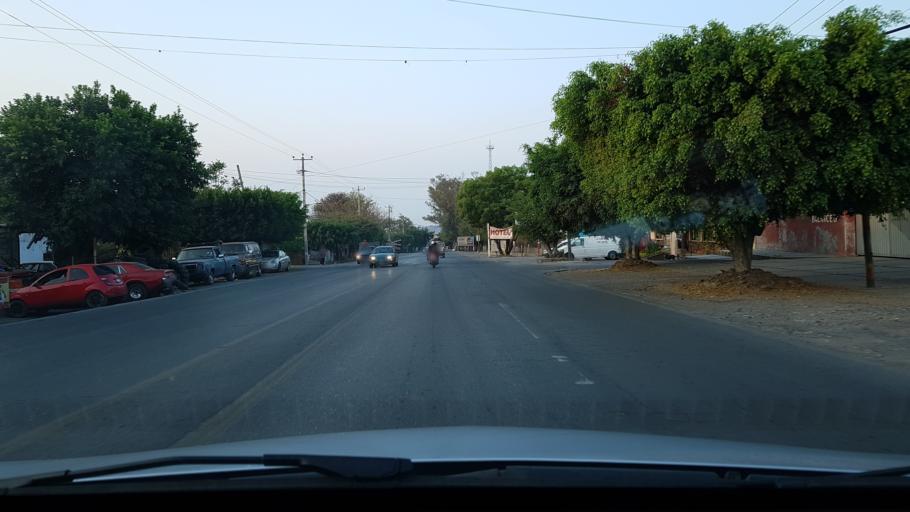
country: MX
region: Morelos
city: Jonacatepec de Leandro Valle
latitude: 18.6901
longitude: -98.8021
